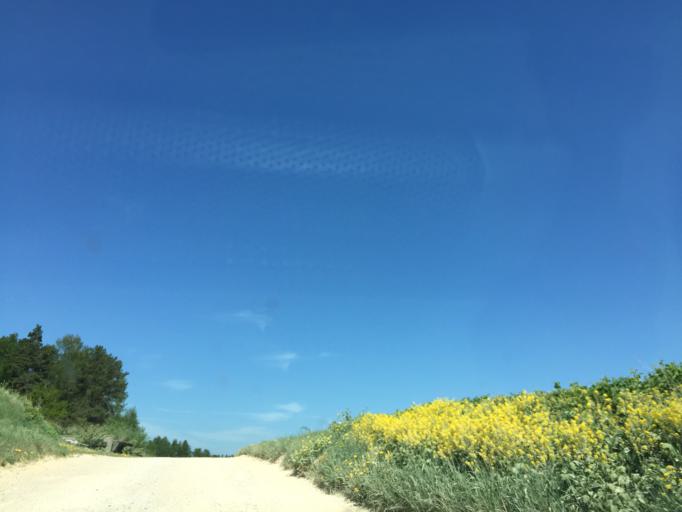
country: LV
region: Ikskile
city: Ikskile
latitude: 56.8652
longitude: 24.5021
